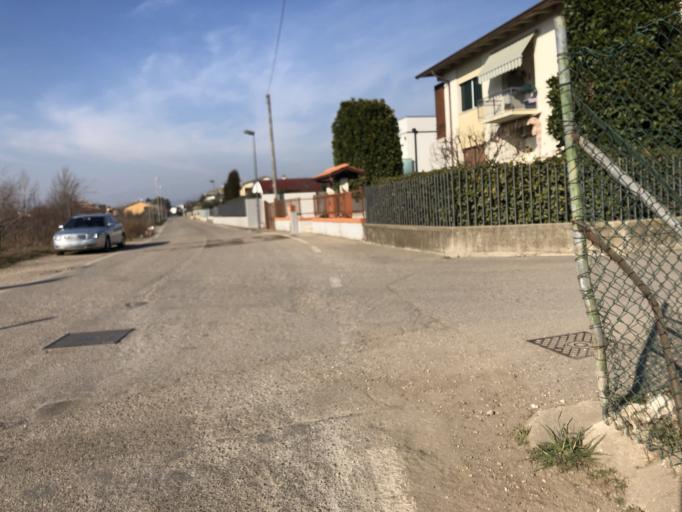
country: IT
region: Veneto
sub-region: Provincia di Verona
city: Lugagnano
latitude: 45.4282
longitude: 10.8817
